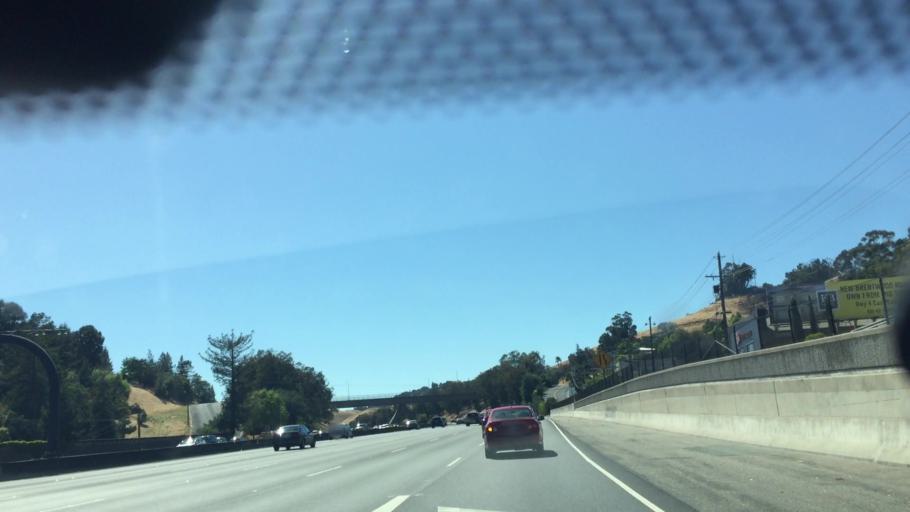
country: US
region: California
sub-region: Contra Costa County
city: Saranap
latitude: 37.8972
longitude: -122.0798
